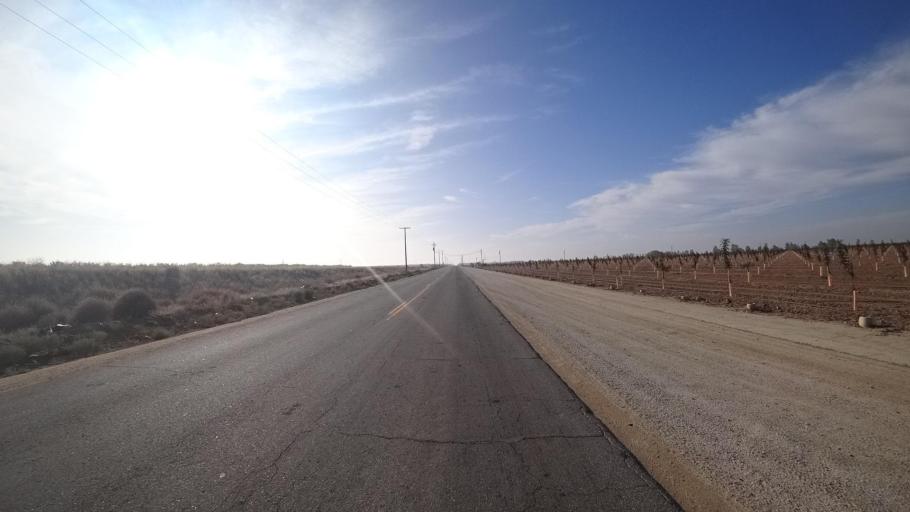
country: US
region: California
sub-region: Kern County
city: McFarland
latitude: 35.6483
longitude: -119.2046
